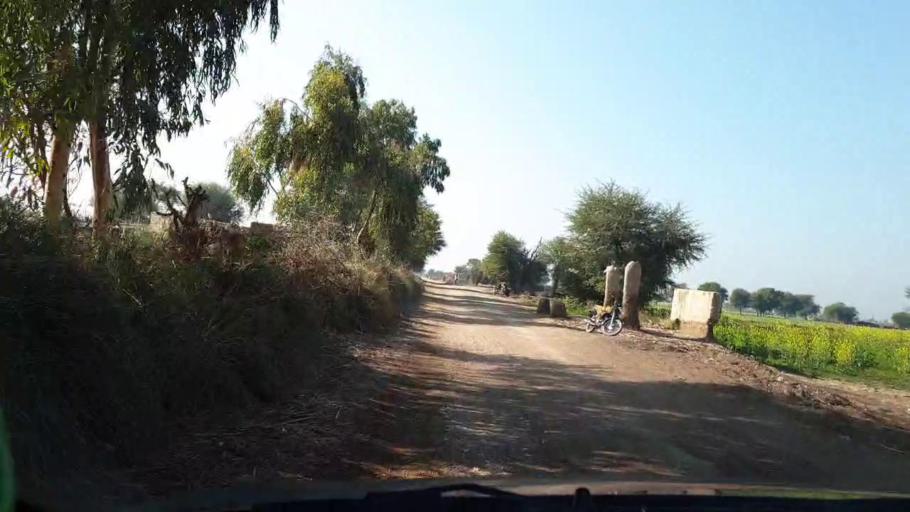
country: PK
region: Sindh
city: Sinjhoro
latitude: 25.9897
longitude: 68.7495
